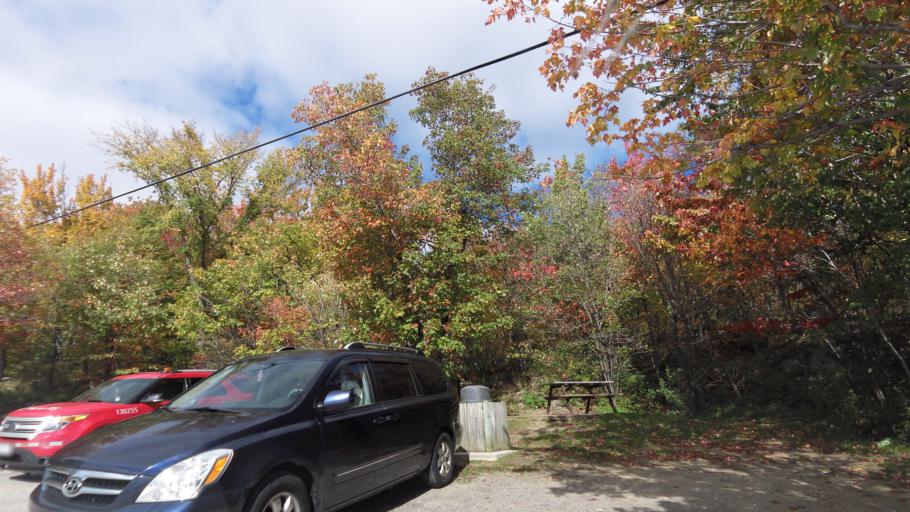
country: CA
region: Ontario
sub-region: Nipissing District
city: North Bay
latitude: 46.3654
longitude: -79.6815
